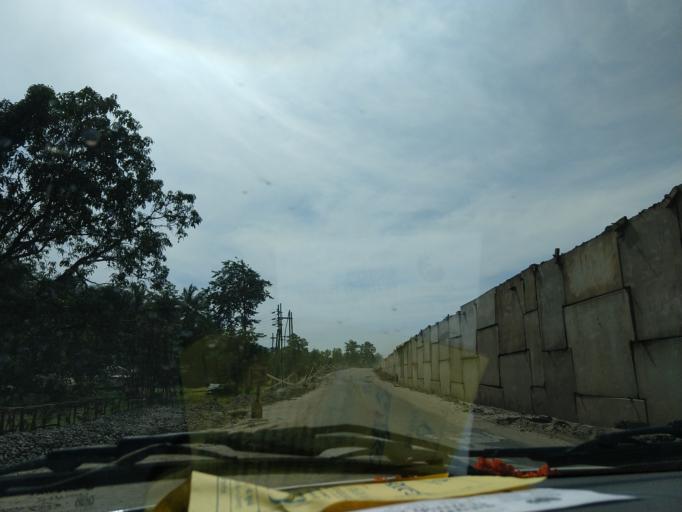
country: IN
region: Maharashtra
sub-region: Sindhudurg
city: Kudal
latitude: 15.9531
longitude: 73.7384
